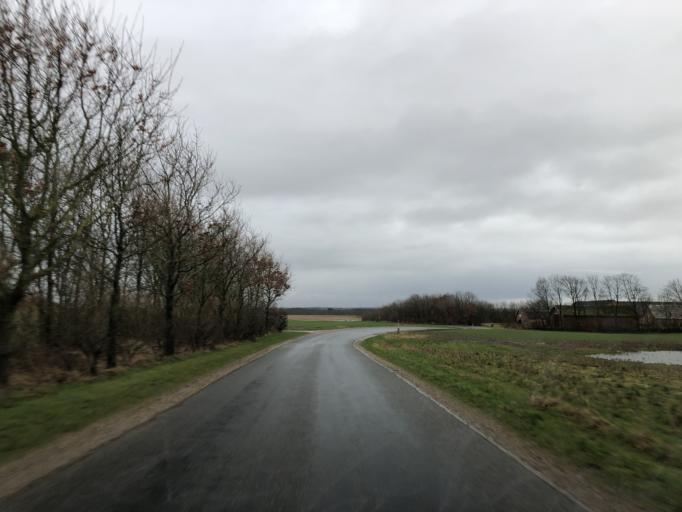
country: DK
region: Central Jutland
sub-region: Holstebro Kommune
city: Holstebro
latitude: 56.3747
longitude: 8.7286
